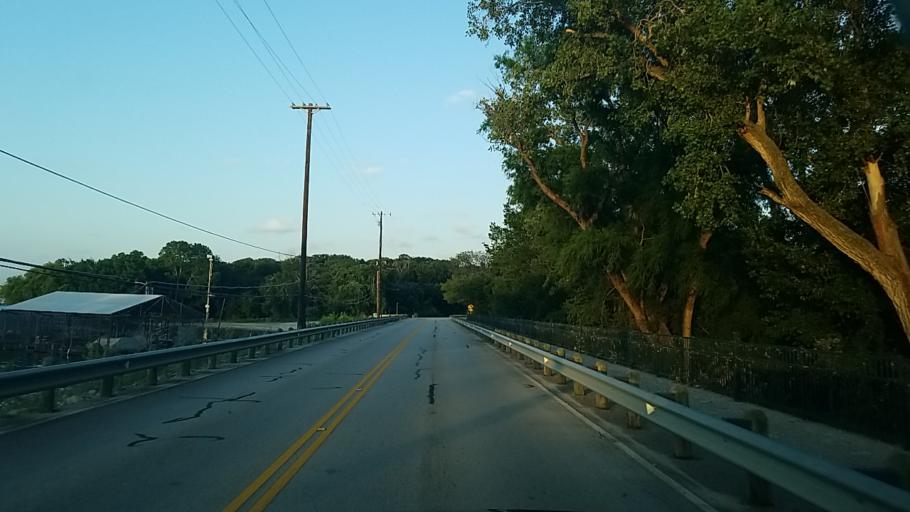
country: US
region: Texas
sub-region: Denton County
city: Highland Village
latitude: 33.0935
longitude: -97.0421
